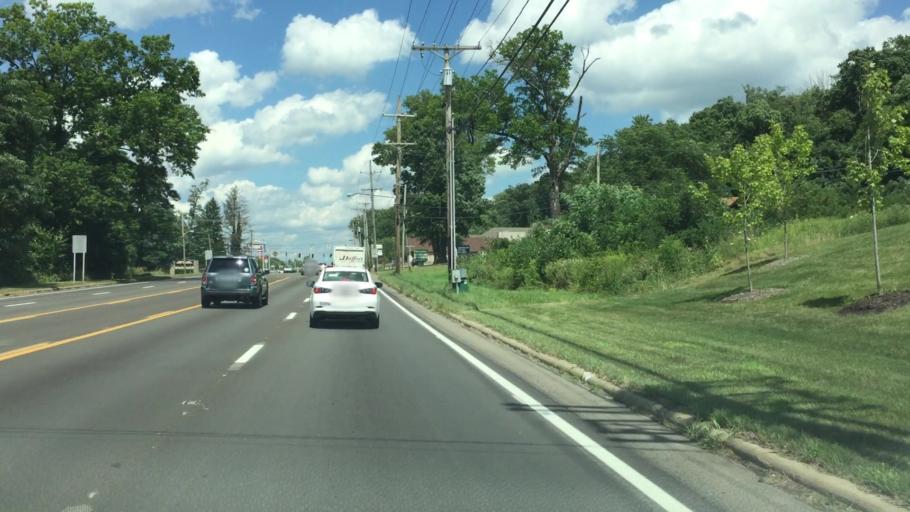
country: US
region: Ohio
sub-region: Trumbull County
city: Howland Center
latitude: 41.2231
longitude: -80.7404
